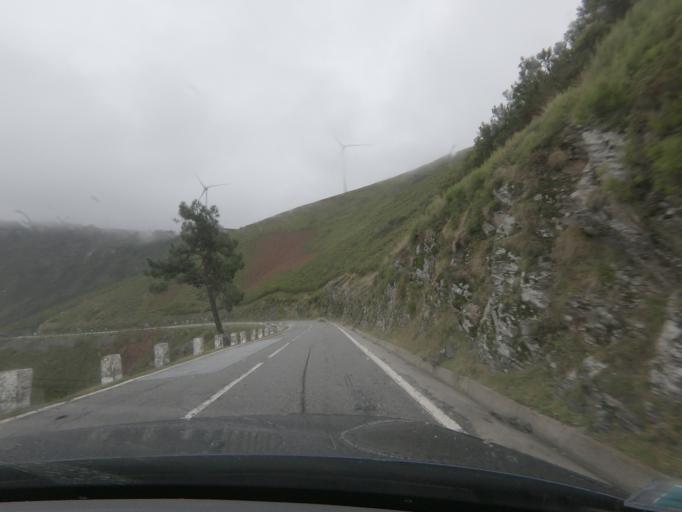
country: PT
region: Vila Real
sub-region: Mondim de Basto
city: Mondim de Basto
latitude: 41.3251
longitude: -7.8831
